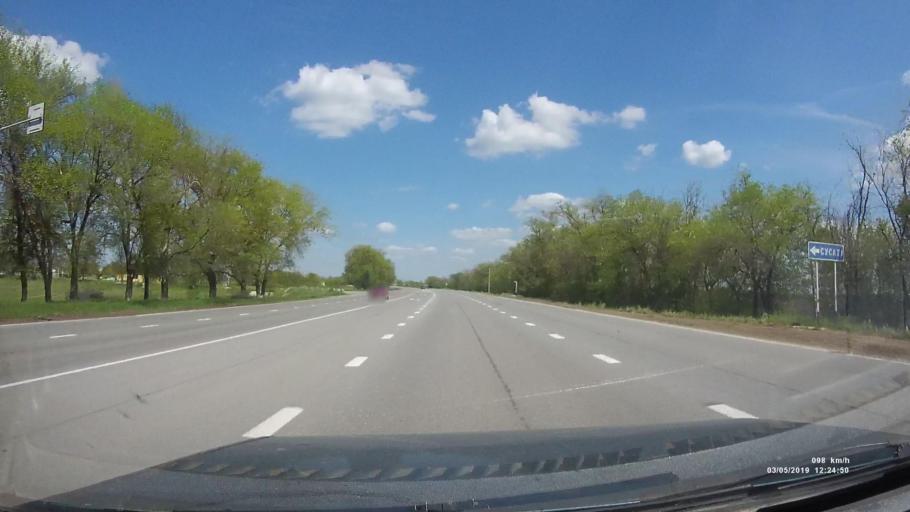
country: RU
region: Rostov
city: Semikarakorsk
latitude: 47.4245
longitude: 40.7052
